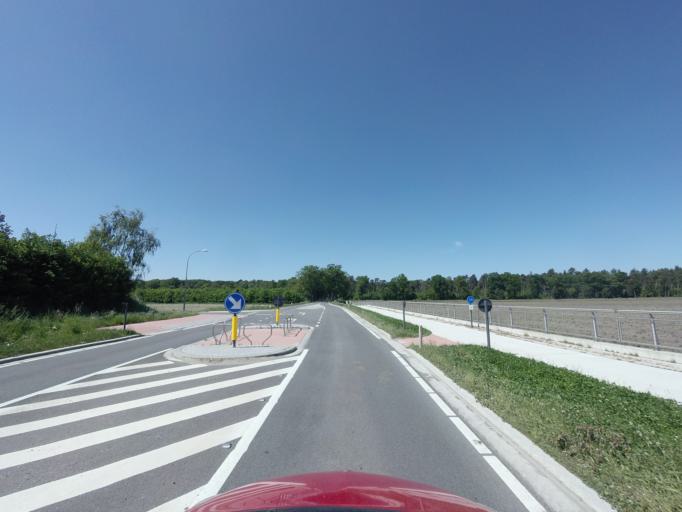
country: BE
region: Flanders
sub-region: Provincie Antwerpen
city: Arendonk
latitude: 51.3680
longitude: 5.0509
